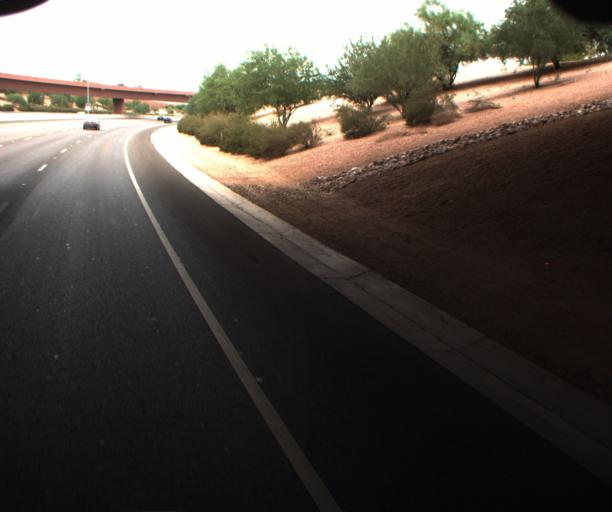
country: US
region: Arizona
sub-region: Maricopa County
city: Mesa
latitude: 33.4657
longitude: -111.7873
